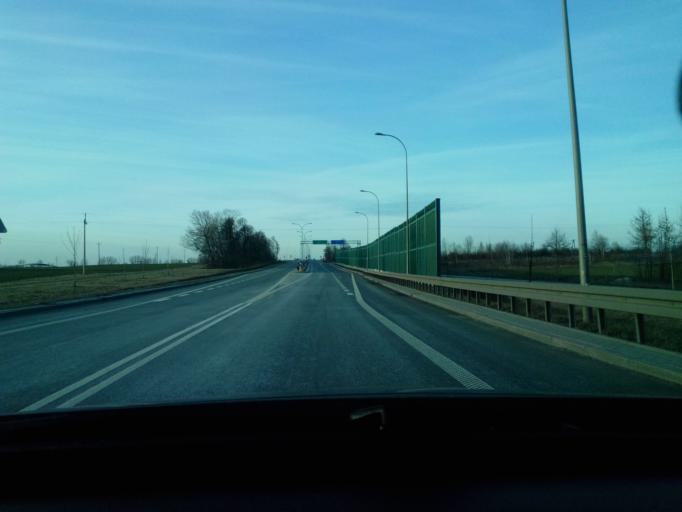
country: PL
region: Kujawsko-Pomorskie
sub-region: Powiat wloclawski
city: Kowal
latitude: 52.4794
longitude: 19.1547
